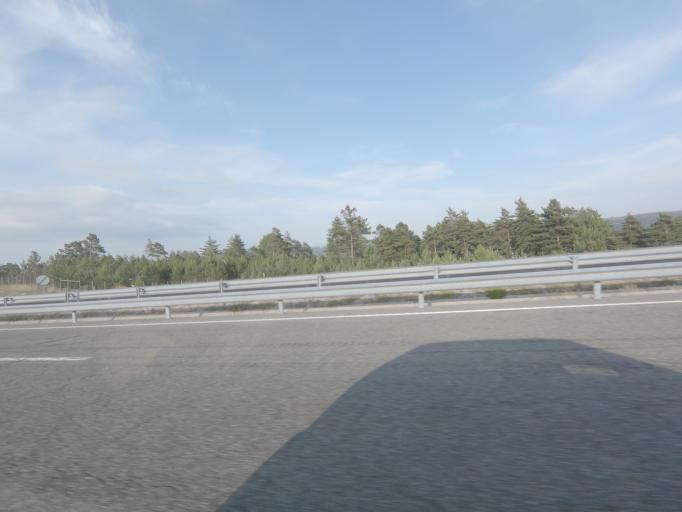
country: PT
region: Vila Real
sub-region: Vila Pouca de Aguiar
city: Vila Pouca de Aguiar
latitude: 41.5124
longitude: -7.6576
